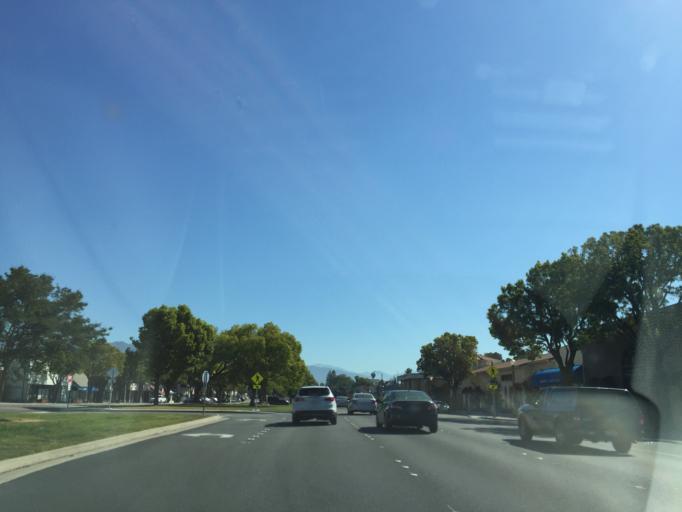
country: US
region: California
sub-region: Los Angeles County
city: San Marino
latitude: 34.1227
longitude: -118.1038
